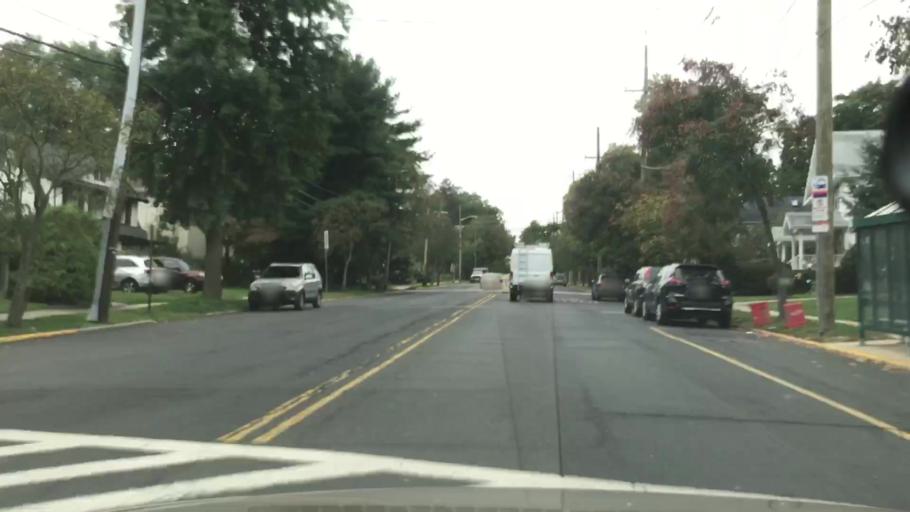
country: US
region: New Jersey
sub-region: Bergen County
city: Leonia
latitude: 40.8692
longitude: -73.9826
